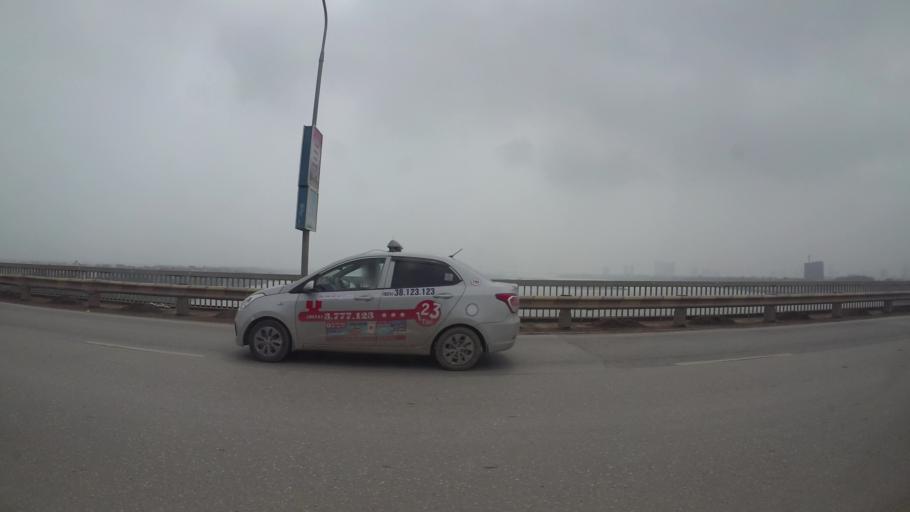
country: VN
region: Ha Noi
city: Tay Ho
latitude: 21.0997
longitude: 105.7866
